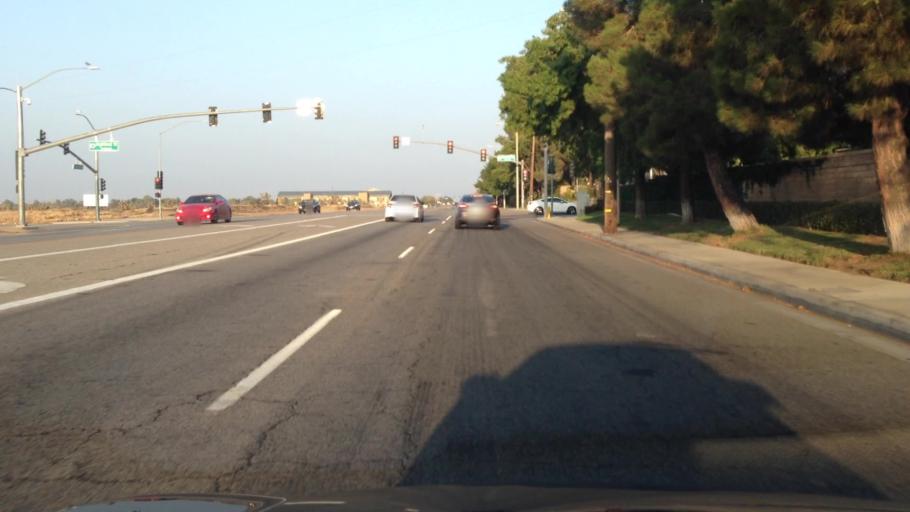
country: US
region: California
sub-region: Los Angeles County
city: Desert View Highlands
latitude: 34.6017
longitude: -118.1753
